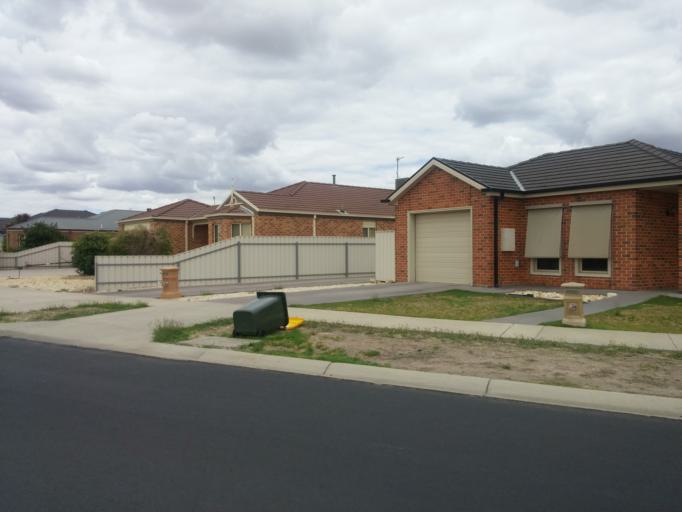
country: AU
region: Victoria
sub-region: Horsham
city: Horsham
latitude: -36.7272
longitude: 142.1993
